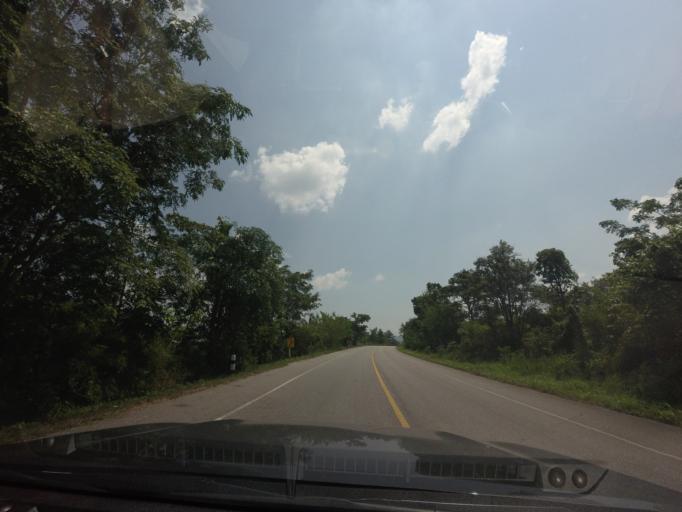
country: TH
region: Uttaradit
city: Thong Saen Khan
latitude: 17.3211
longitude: 100.3883
